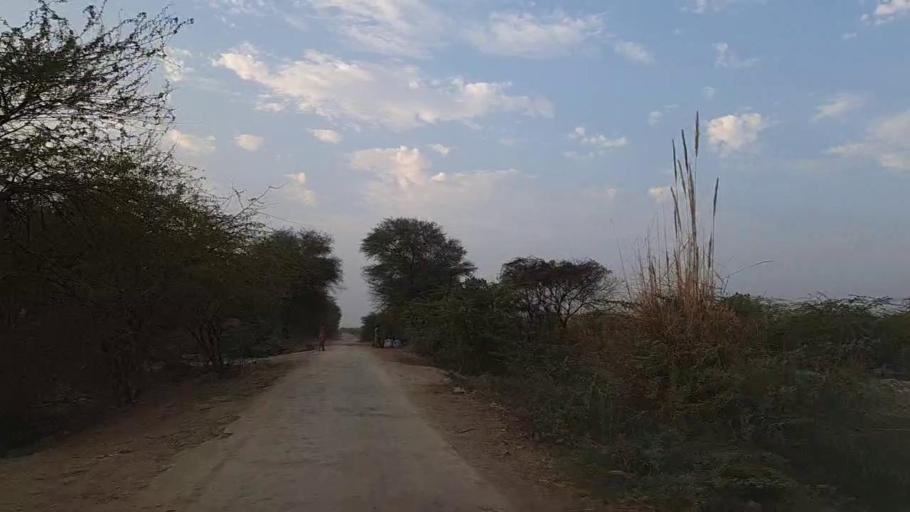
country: PK
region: Sindh
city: Mirwah Gorchani
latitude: 25.3414
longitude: 69.2067
